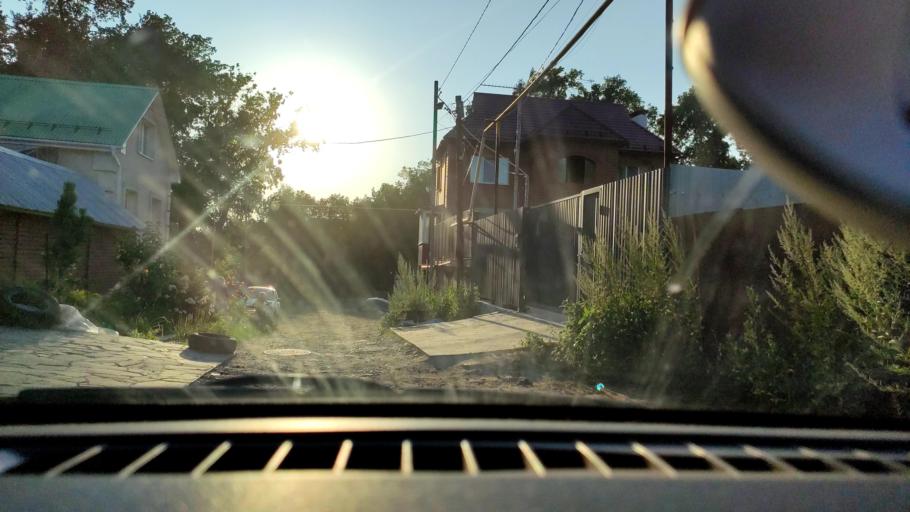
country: RU
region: Samara
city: Samara
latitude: 53.2752
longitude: 50.2081
